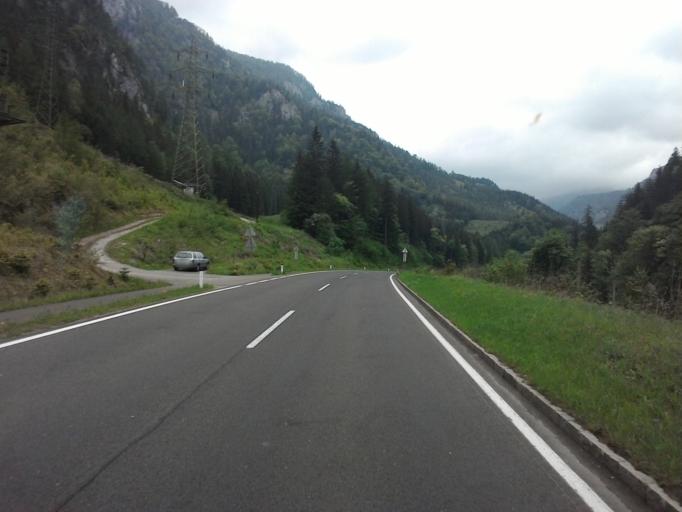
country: AT
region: Styria
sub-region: Politischer Bezirk Leoben
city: Eisenerz
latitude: 47.5732
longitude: 14.8359
